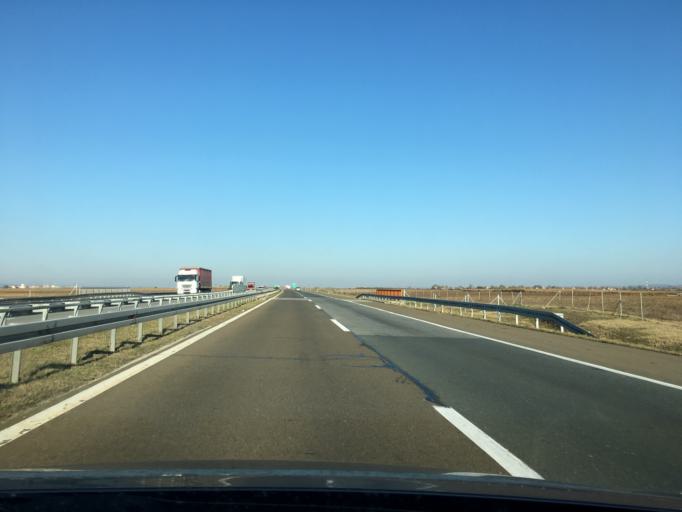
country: RS
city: Novi Karlovci
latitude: 45.0539
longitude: 20.1705
